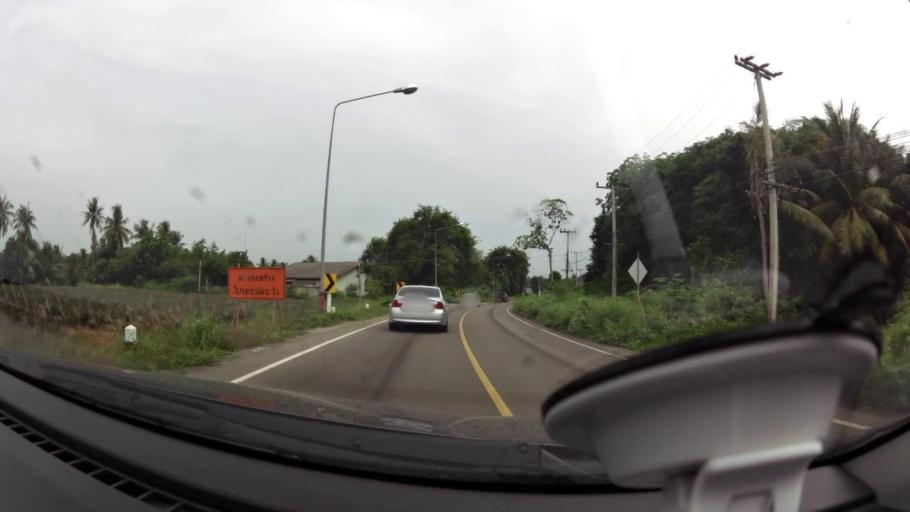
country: TH
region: Prachuap Khiri Khan
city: Pran Buri
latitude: 12.4290
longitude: 99.9585
